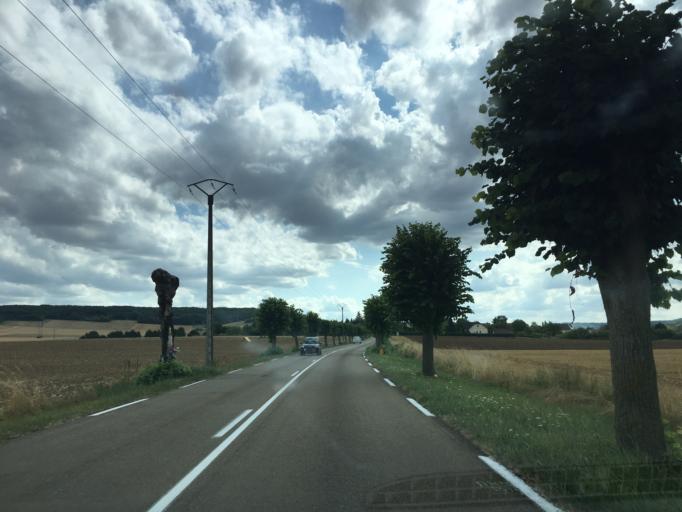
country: FR
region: Bourgogne
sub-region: Departement de l'Yonne
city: Joigny
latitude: 47.9605
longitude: 3.3805
